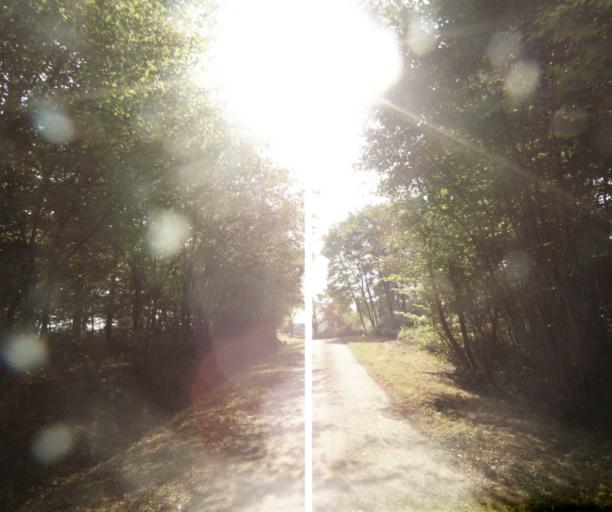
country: FR
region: Bourgogne
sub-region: Departement de Saone-et-Loire
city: Palinges
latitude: 46.5066
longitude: 4.2245
